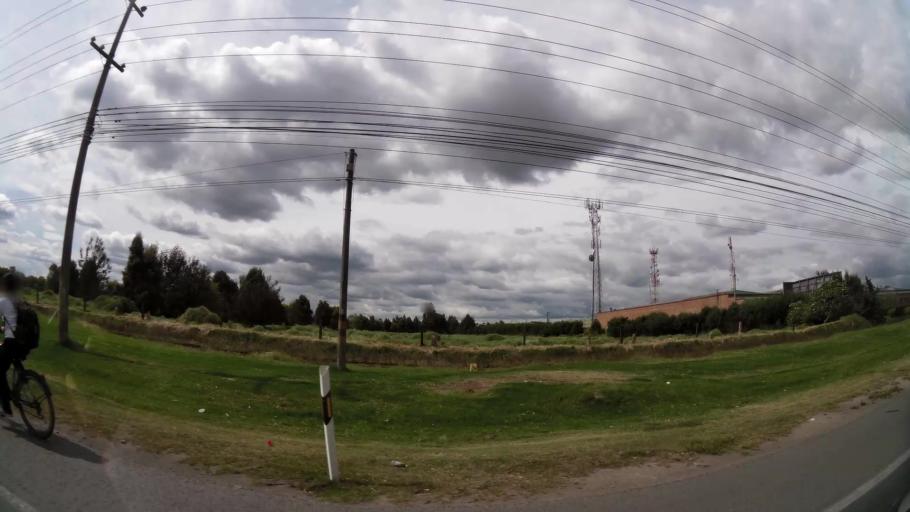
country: CO
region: Cundinamarca
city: Funza
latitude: 4.6990
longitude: -74.1867
